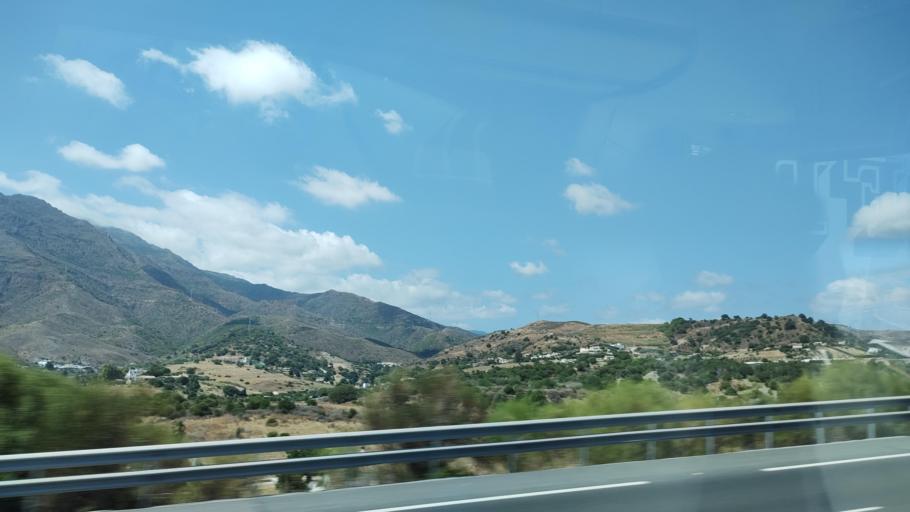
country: ES
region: Andalusia
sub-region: Provincia de Malaga
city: Estepona
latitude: 36.4337
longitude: -5.1806
